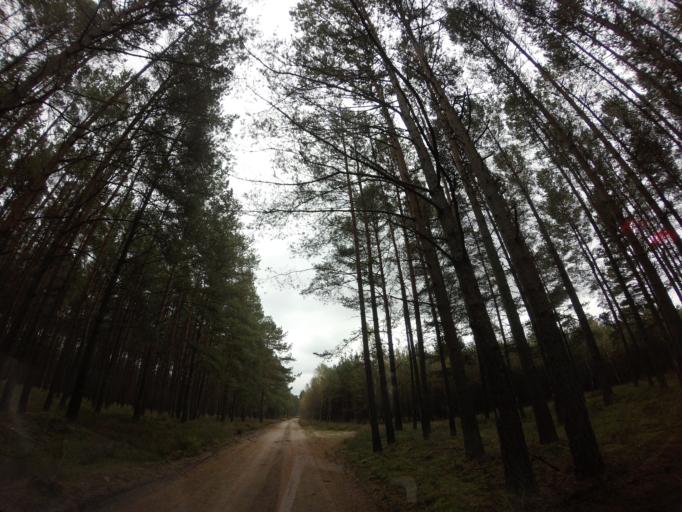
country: PL
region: West Pomeranian Voivodeship
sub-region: Powiat choszczenski
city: Drawno
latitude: 53.1353
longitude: 15.7626
